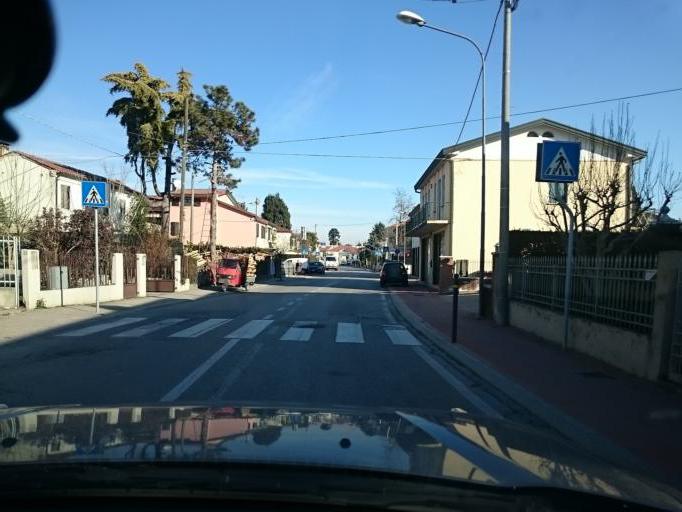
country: IT
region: Veneto
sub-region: Provincia di Venezia
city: Vigonovo
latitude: 45.3842
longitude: 12.0060
